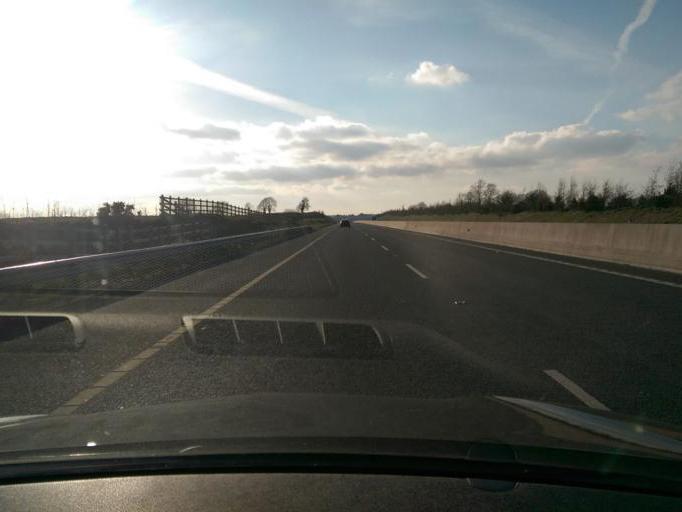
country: IE
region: Leinster
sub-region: Laois
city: Rathdowney
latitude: 52.9191
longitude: -7.5587
